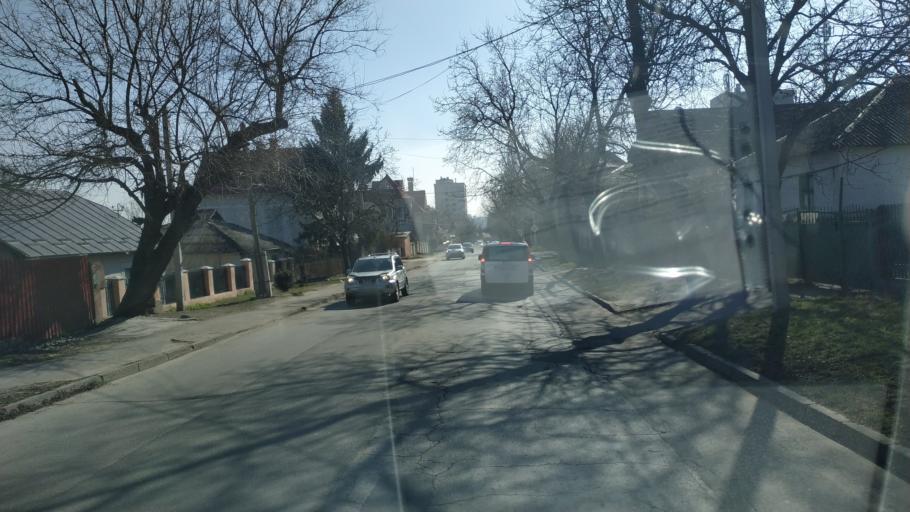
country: MD
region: Chisinau
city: Chisinau
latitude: 47.0330
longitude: 28.7981
